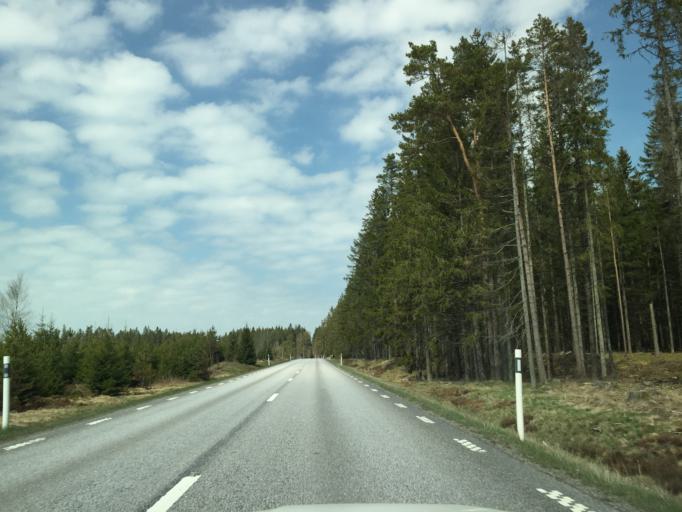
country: SE
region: Vaestra Goetaland
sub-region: Bengtsfors Kommun
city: Dals Langed
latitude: 58.8184
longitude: 12.1424
